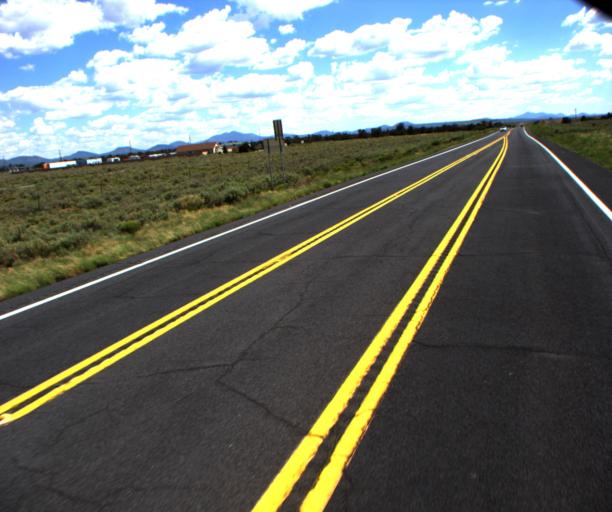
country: US
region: Arizona
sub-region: Coconino County
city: Grand Canyon Village
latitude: 35.6480
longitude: -112.1401
